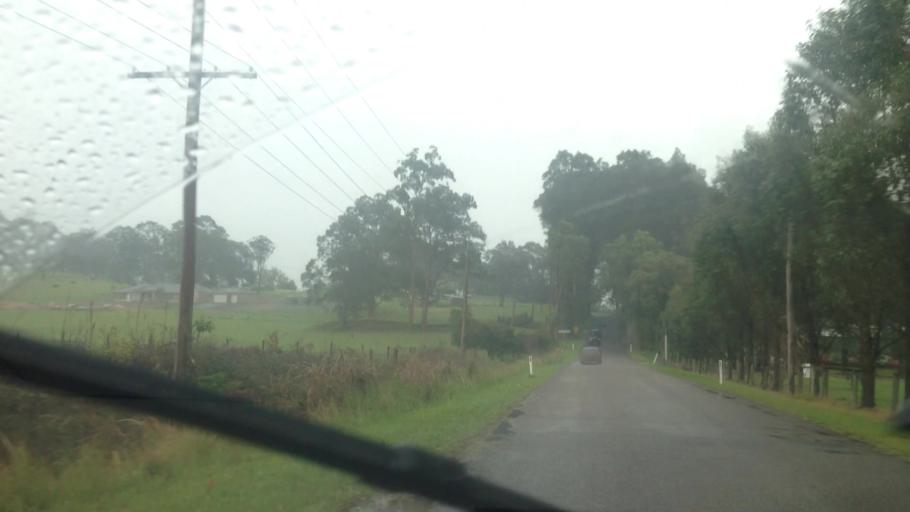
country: AU
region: New South Wales
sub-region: Wyong Shire
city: Little Jilliby
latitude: -33.2038
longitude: 151.3637
